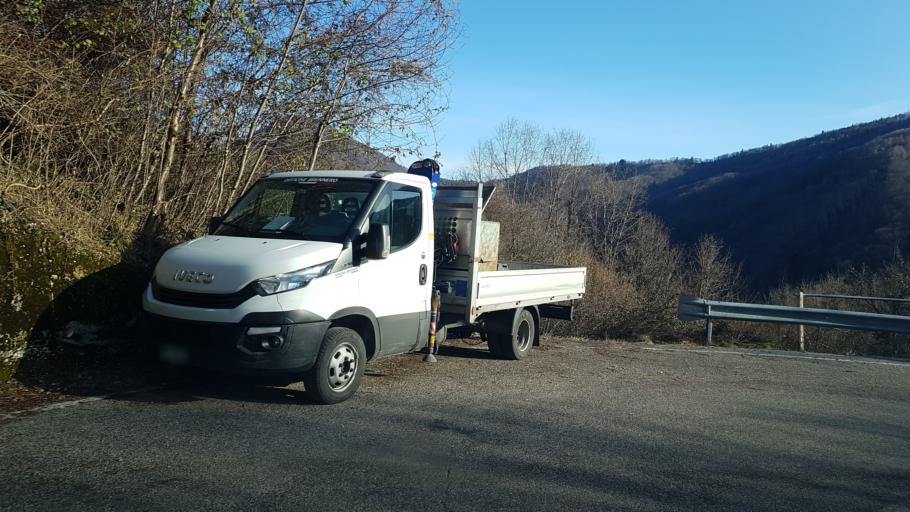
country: IT
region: Friuli Venezia Giulia
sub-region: Provincia di Udine
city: Clodig
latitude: 46.1583
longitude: 13.5880
